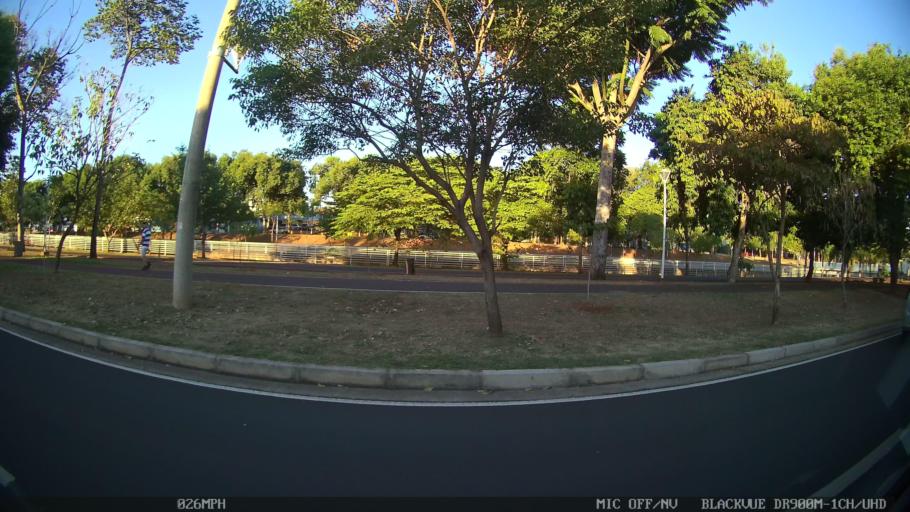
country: BR
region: Sao Paulo
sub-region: Sao Jose Do Rio Preto
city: Sao Jose do Rio Preto
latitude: -20.7897
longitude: -49.3769
